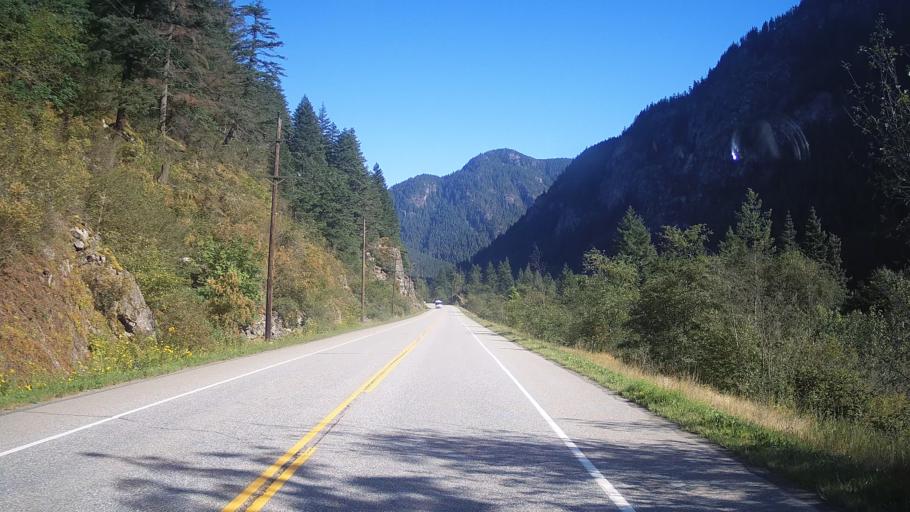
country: CA
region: British Columbia
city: Hope
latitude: 49.5837
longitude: -121.4038
